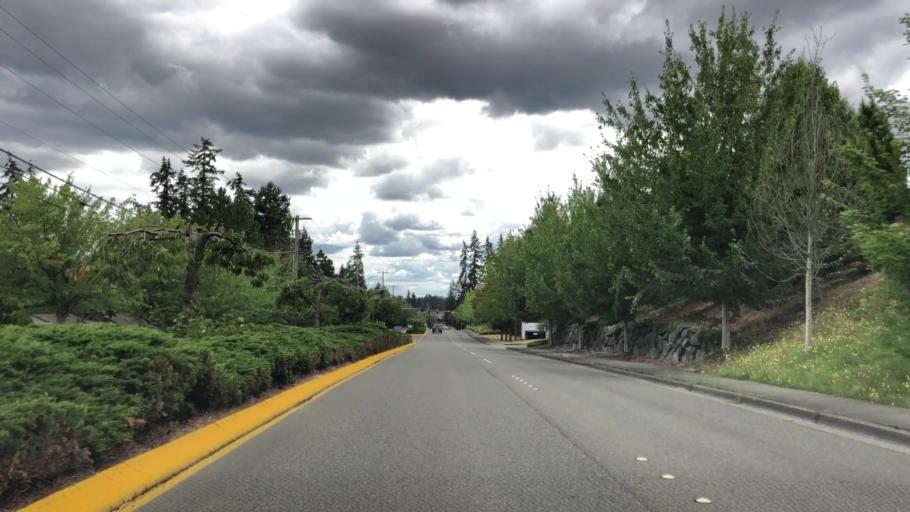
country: US
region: Washington
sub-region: Snohomish County
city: Alderwood Manor
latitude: 47.8305
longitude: -122.2818
